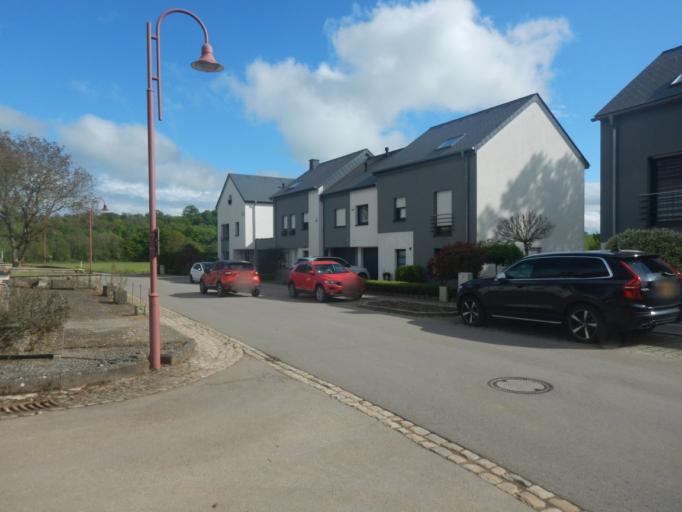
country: LU
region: Luxembourg
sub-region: Canton d'Esch-sur-Alzette
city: Reckange-sur-Mess
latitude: 49.5491
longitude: 6.0030
